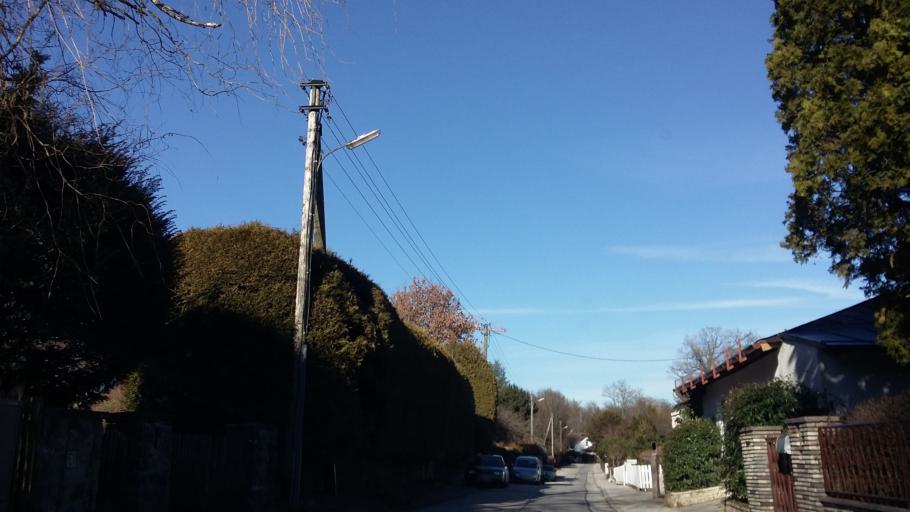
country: DE
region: Bavaria
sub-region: Upper Bavaria
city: Pocking
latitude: 47.9636
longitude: 11.3072
